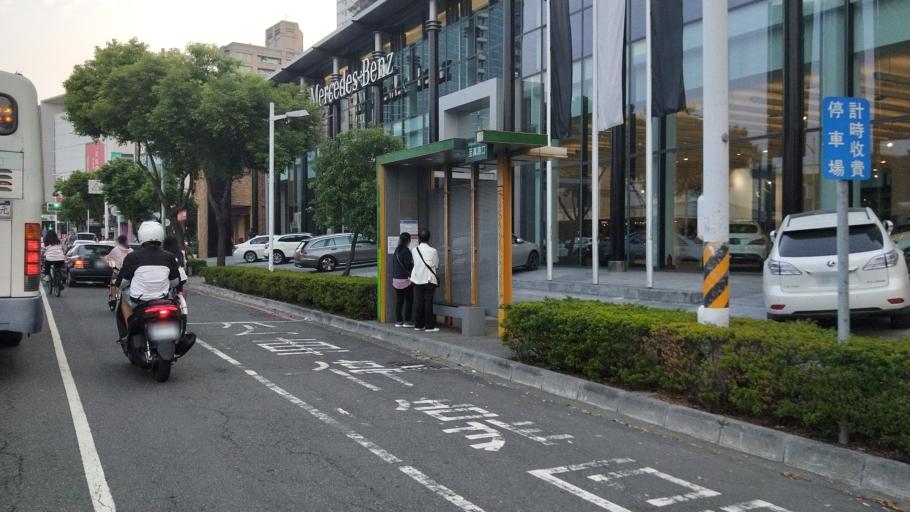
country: TW
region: Kaohsiung
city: Kaohsiung
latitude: 22.6725
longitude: 120.3042
